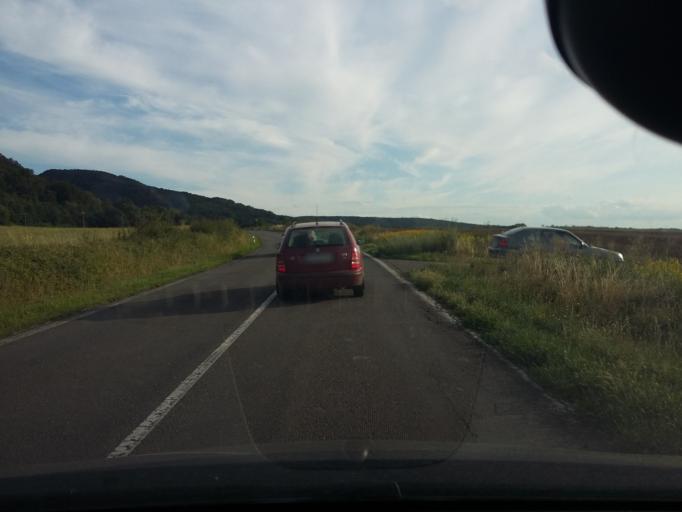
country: SK
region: Bratislavsky
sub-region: Okres Malacky
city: Malacky
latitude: 48.3777
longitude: 17.1494
